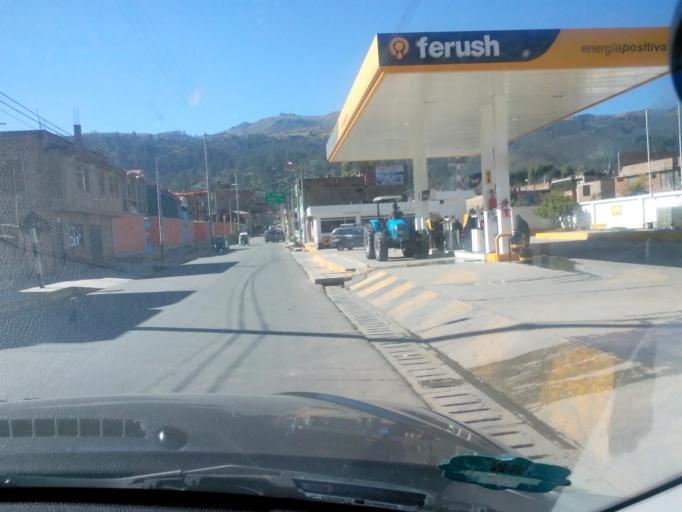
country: PE
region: Apurimac
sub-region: Provincia de Andahuaylas
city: Talavera
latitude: -13.6589
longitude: -73.4307
